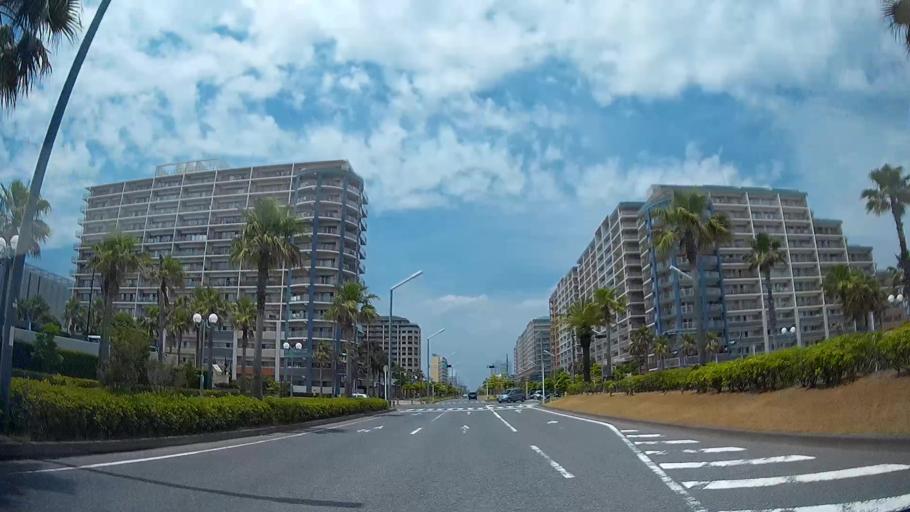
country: JP
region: Tokyo
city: Urayasu
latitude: 35.6391
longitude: 139.9286
